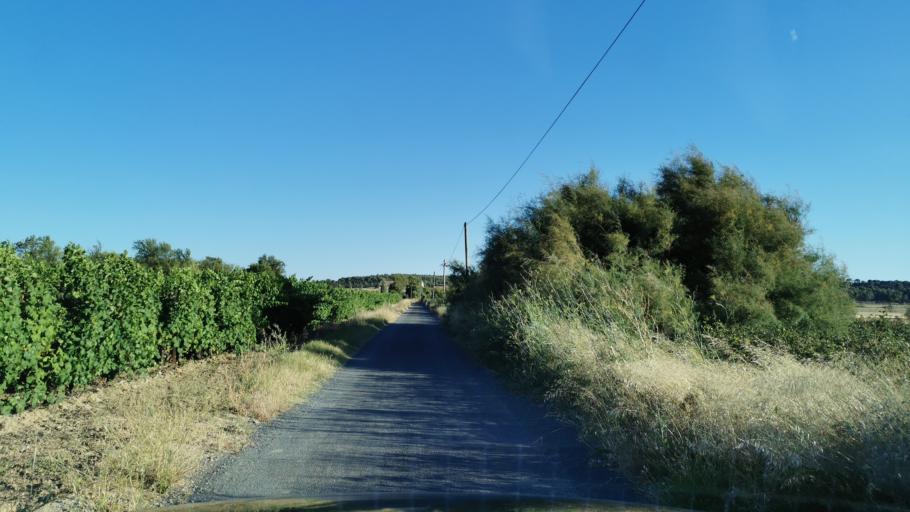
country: FR
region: Languedoc-Roussillon
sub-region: Departement de l'Aude
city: Ouveillan
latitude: 43.2823
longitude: 2.9759
